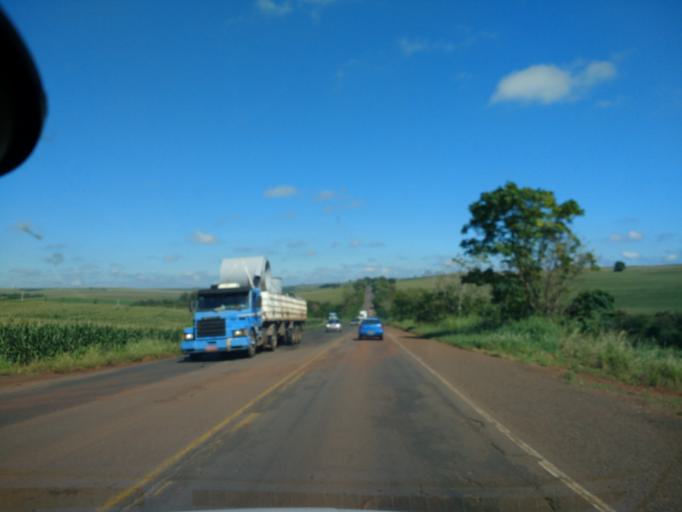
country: BR
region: Parana
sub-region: Terra Boa
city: Terra Boa
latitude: -23.6129
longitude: -52.4266
